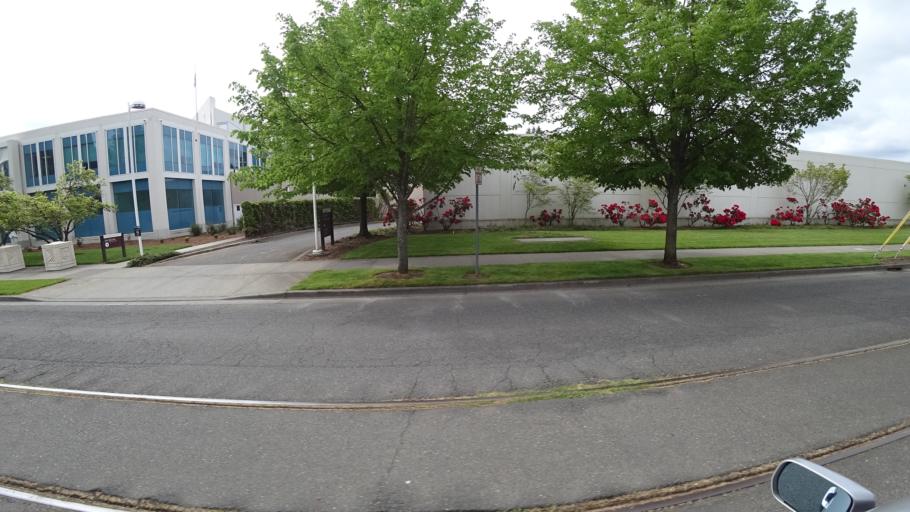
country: US
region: Oregon
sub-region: Washington County
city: Hillsboro
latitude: 45.5215
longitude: -122.9926
